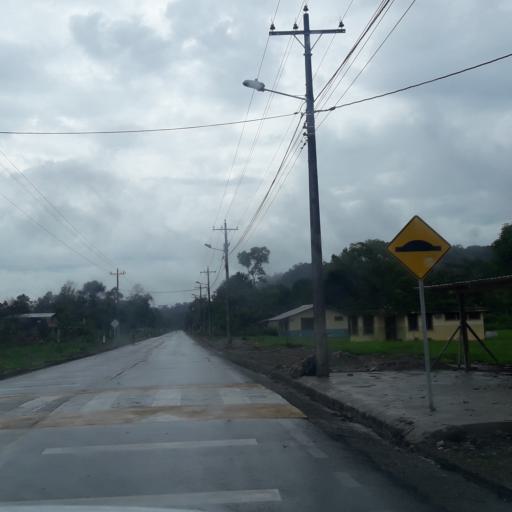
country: EC
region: Napo
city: Tena
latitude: -1.0659
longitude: -77.6418
